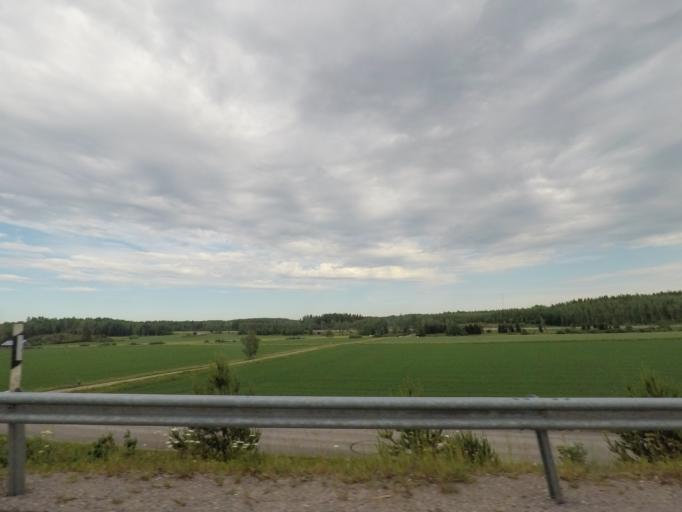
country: FI
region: Uusimaa
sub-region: Helsinki
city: Maentsaelae
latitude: 60.6787
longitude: 25.3589
